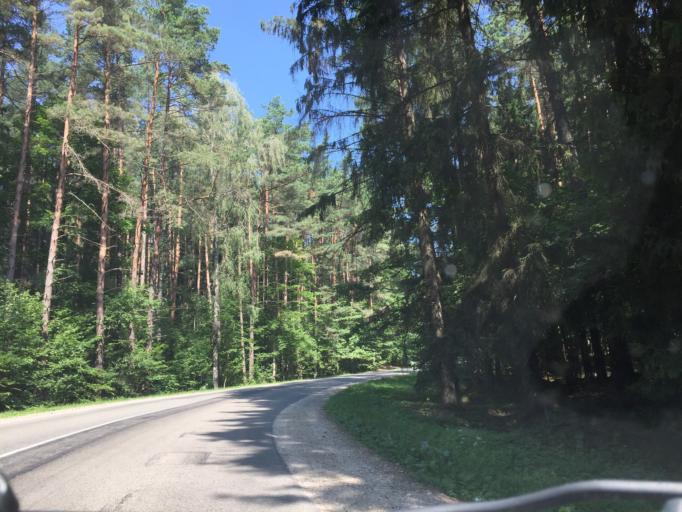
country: LV
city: Tervete
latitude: 56.4842
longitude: 23.3733
